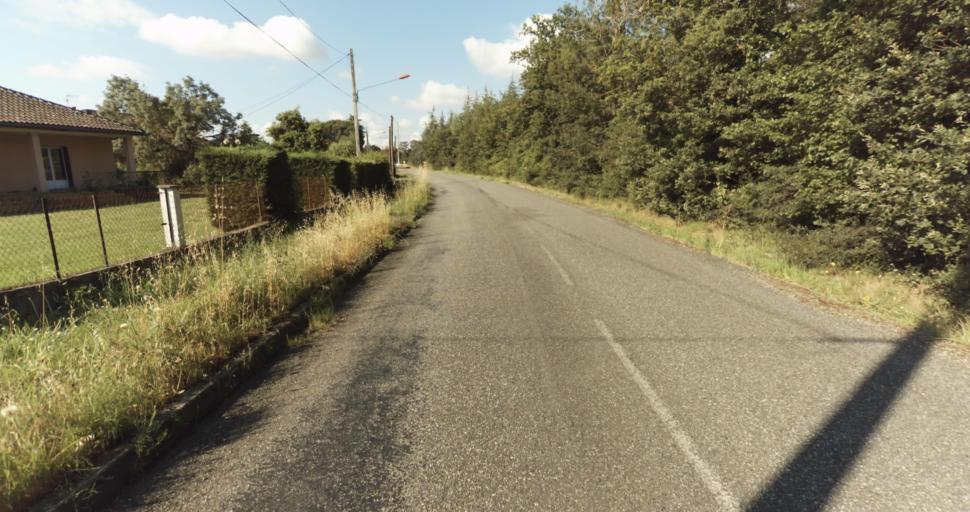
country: FR
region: Midi-Pyrenees
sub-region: Departement de la Haute-Garonne
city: Fontenilles
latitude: 43.5676
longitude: 1.1975
